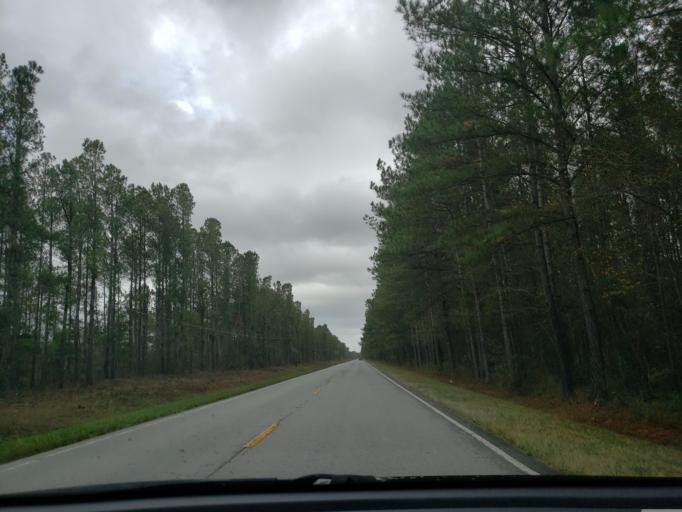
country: US
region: North Carolina
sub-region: Onslow County
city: Half Moon
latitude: 34.7254
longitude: -77.6054
